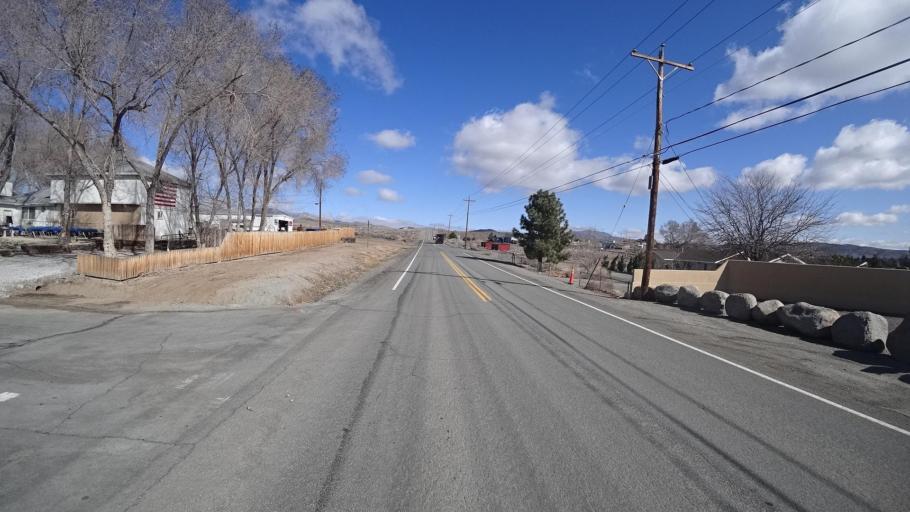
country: US
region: Nevada
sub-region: Washoe County
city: Cold Springs
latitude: 39.6647
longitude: -119.9224
